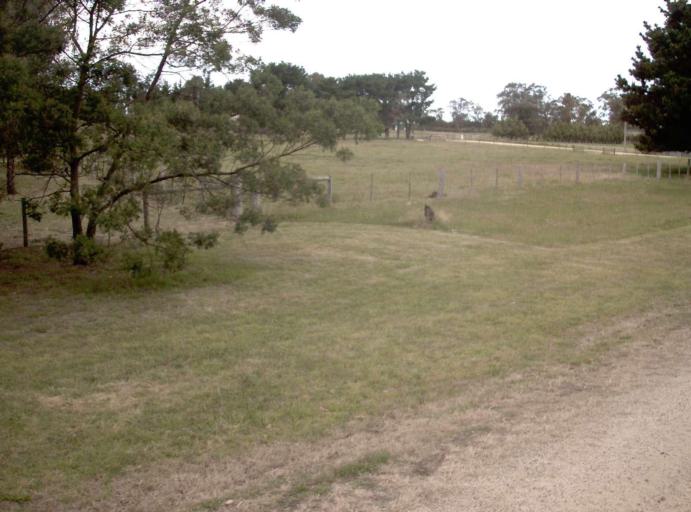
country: AU
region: Victoria
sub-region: Wellington
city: Sale
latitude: -38.1827
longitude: 147.0908
